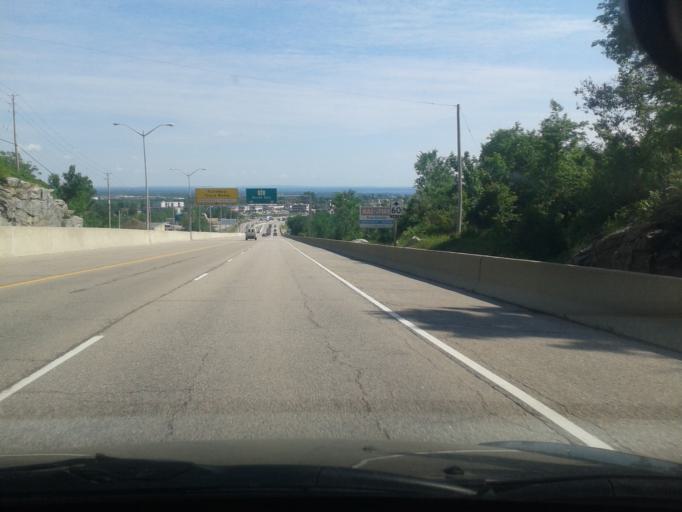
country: CA
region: Ontario
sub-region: Nipissing District
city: North Bay
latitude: 46.3412
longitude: -79.4697
